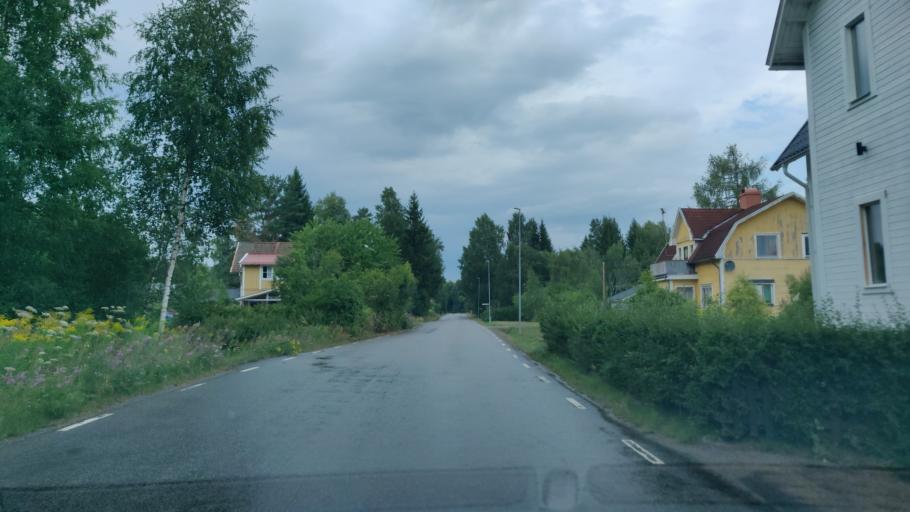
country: SE
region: Vaermland
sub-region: Munkfors Kommun
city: Munkfors
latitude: 59.8555
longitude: 13.5536
